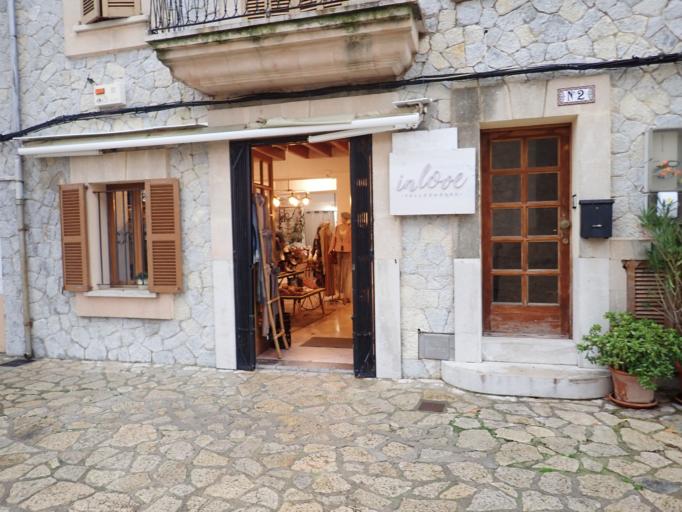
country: ES
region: Balearic Islands
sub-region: Illes Balears
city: Valldemossa
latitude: 39.7096
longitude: 2.6225
